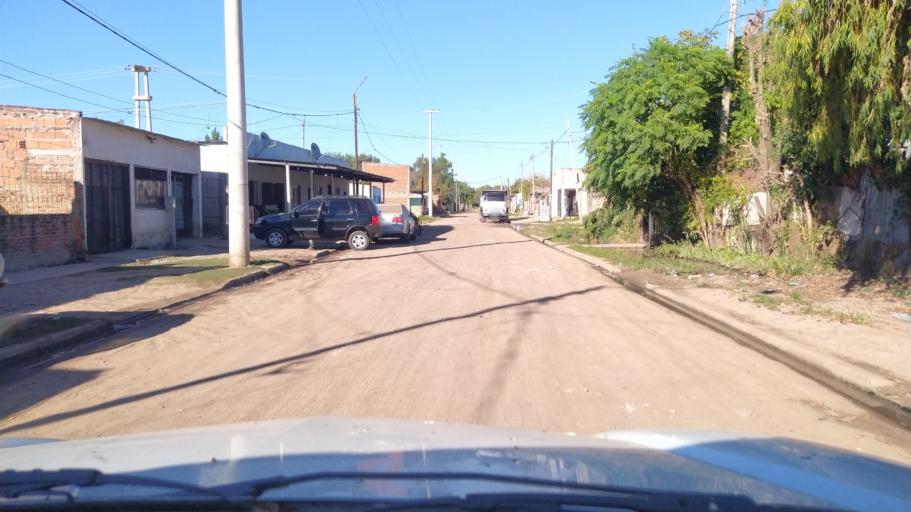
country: AR
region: Corrientes
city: Corrientes
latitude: -27.4952
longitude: -58.8092
